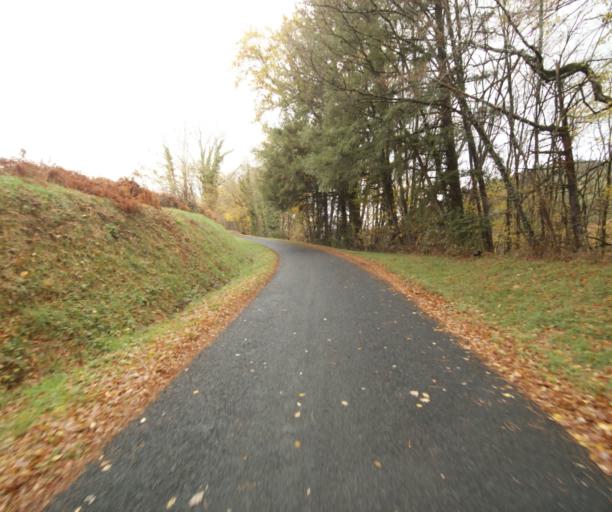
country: FR
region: Limousin
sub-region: Departement de la Correze
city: Cornil
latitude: 45.2029
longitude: 1.6585
